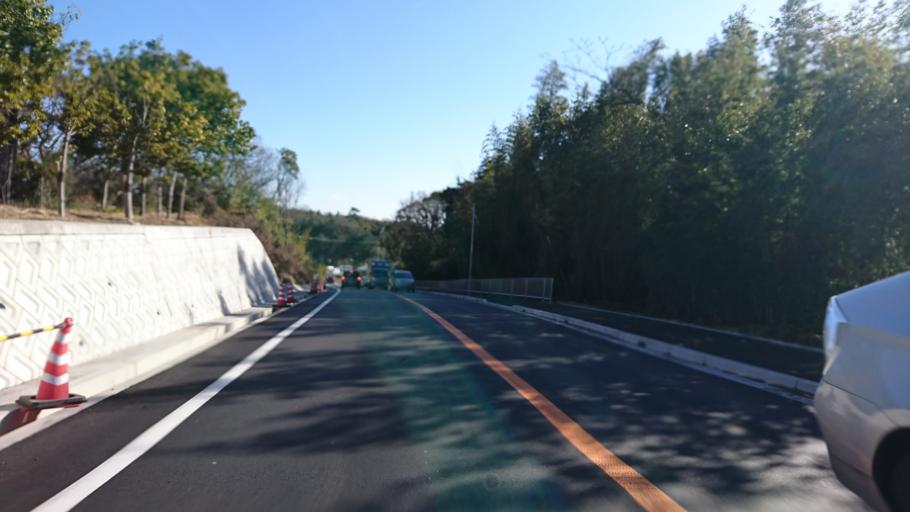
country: JP
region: Hyogo
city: Miki
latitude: 34.7174
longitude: 134.9631
